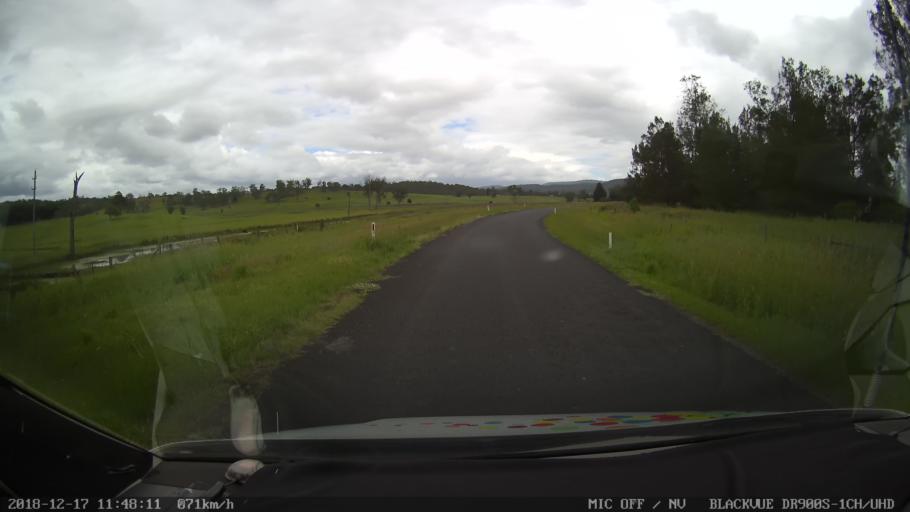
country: AU
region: New South Wales
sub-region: Kyogle
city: Kyogle
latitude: -28.6198
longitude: 152.5904
